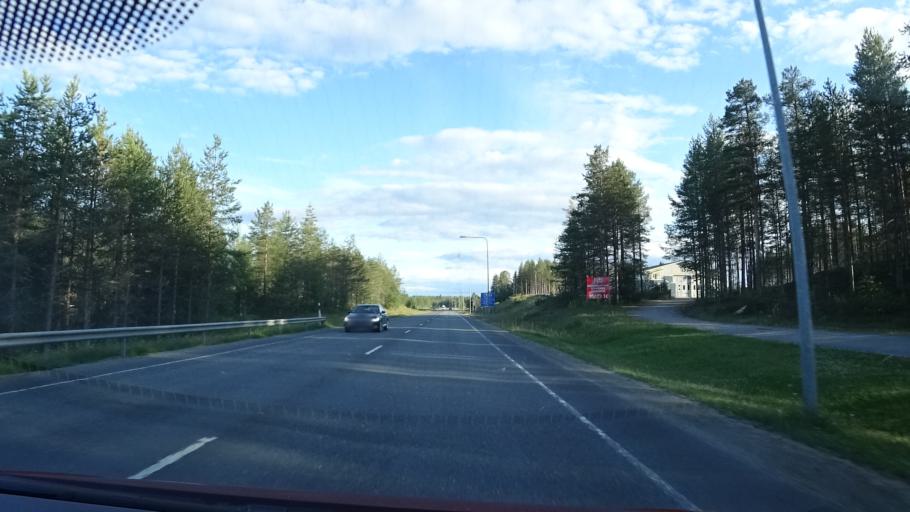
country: FI
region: Northern Ostrobothnia
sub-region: Koillismaa
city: Kuusamo
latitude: 66.0030
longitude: 29.1523
